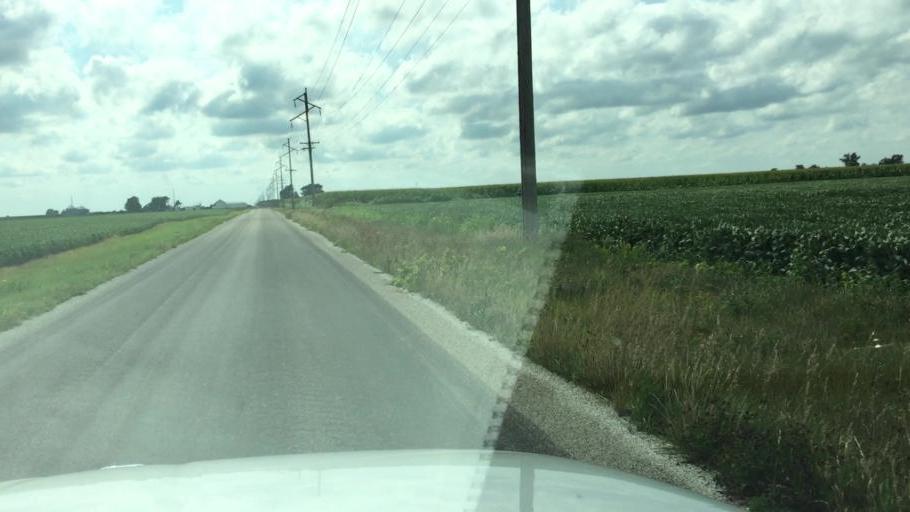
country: US
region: Illinois
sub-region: Hancock County
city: Carthage
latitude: 40.4168
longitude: -91.1676
